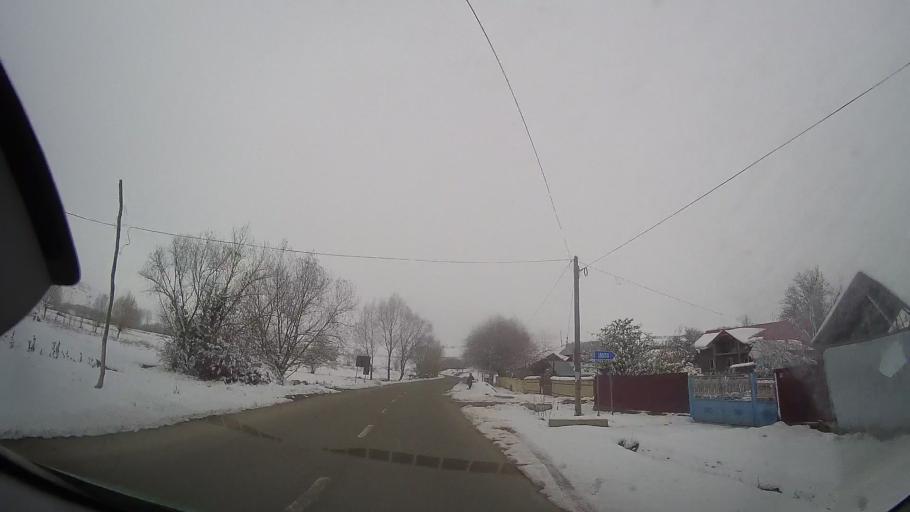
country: RO
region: Neamt
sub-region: Comuna Oniceni
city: Oniceni
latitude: 46.8009
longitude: 27.1381
